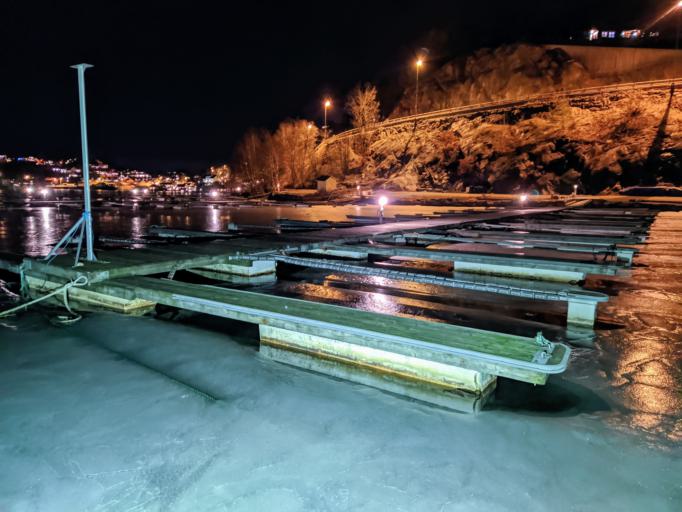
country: NO
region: Aust-Agder
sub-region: Arendal
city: Arendal
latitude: 58.4399
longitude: 8.7392
